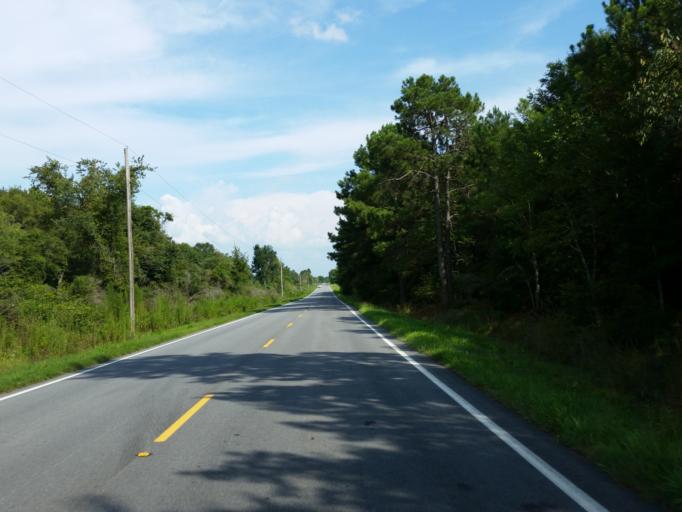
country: US
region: Georgia
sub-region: Turner County
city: Ashburn
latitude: 31.8119
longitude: -83.7208
